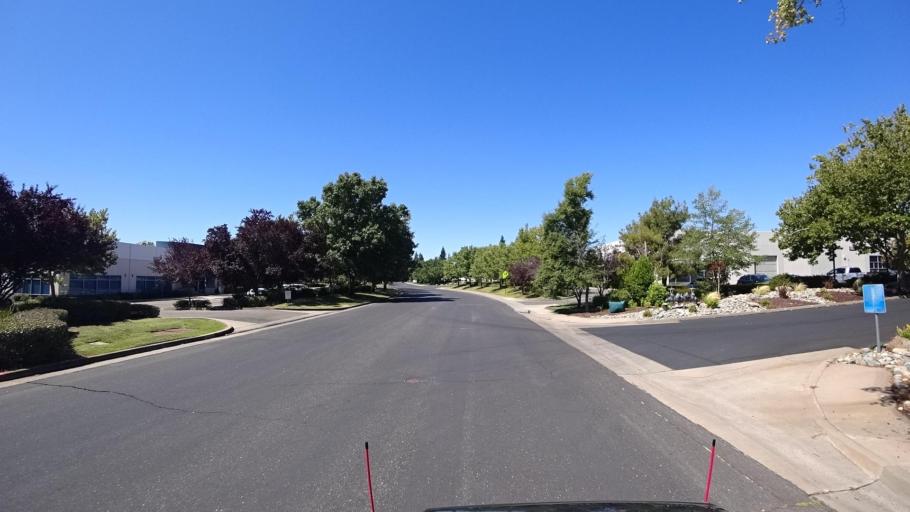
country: US
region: California
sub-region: Placer County
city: Roseville
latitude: 38.8135
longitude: -121.2962
